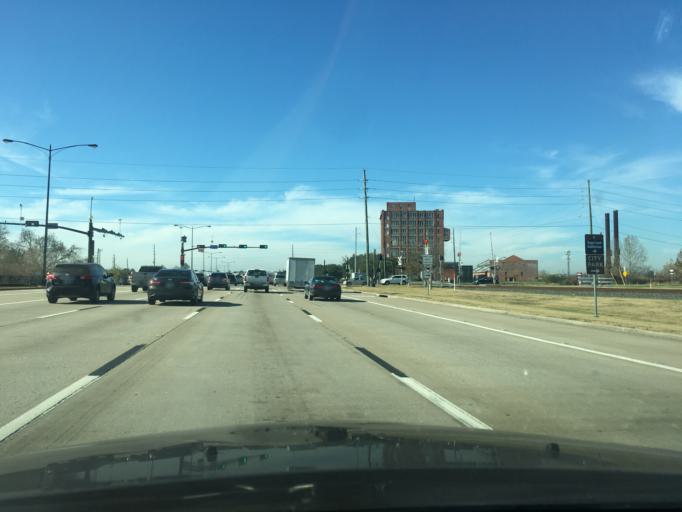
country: US
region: Texas
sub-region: Fort Bend County
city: Sugar Land
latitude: 29.6206
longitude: -95.6319
